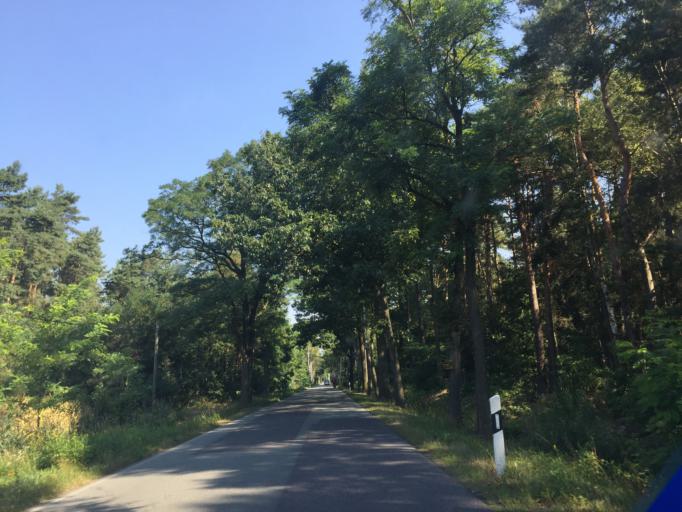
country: DE
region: Saxony
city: Uhyst
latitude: 51.3536
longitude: 14.5066
